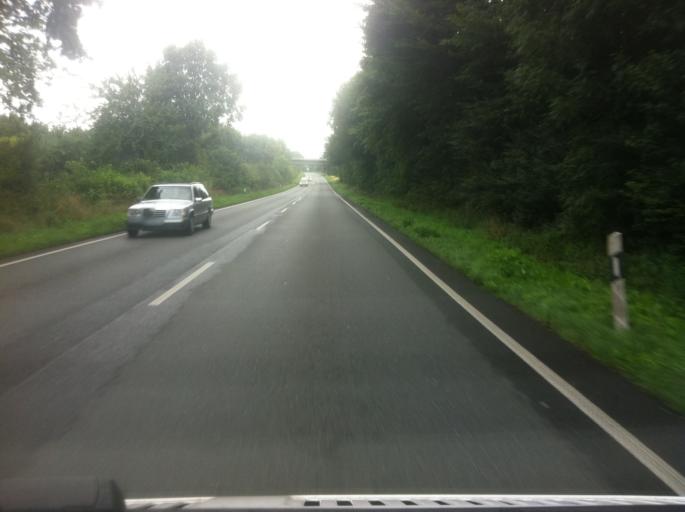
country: DE
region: North Rhine-Westphalia
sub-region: Regierungsbezirk Dusseldorf
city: Goch
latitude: 51.6815
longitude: 6.1259
